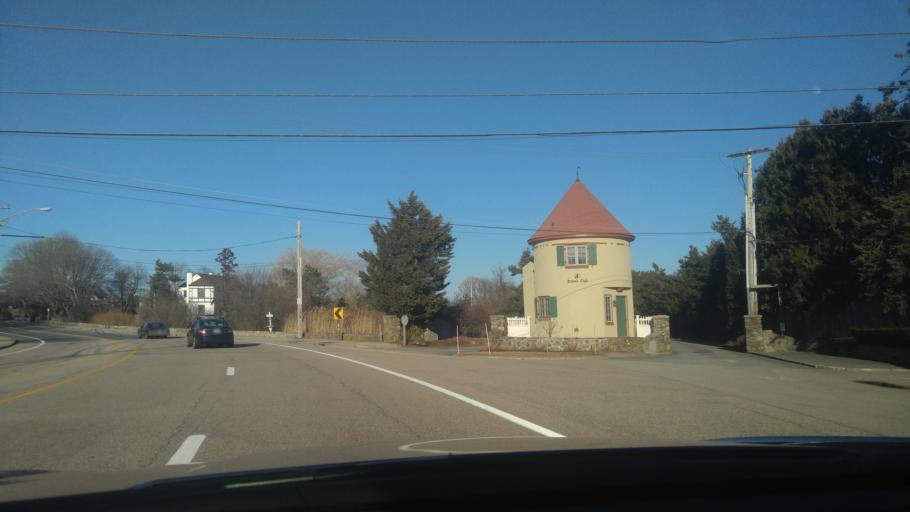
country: US
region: Rhode Island
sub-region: Washington County
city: Narragansett Pier
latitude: 41.4391
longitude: -71.4515
